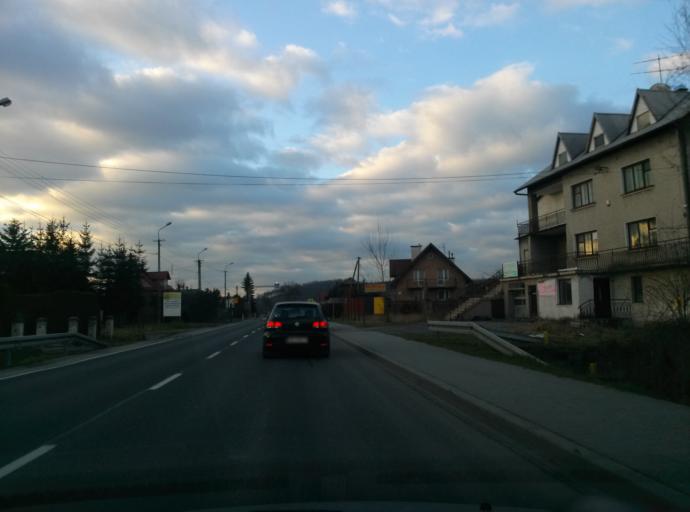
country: PL
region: Lesser Poland Voivodeship
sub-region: Powiat brzeski
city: Gnojnik
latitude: 49.9172
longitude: 20.5985
